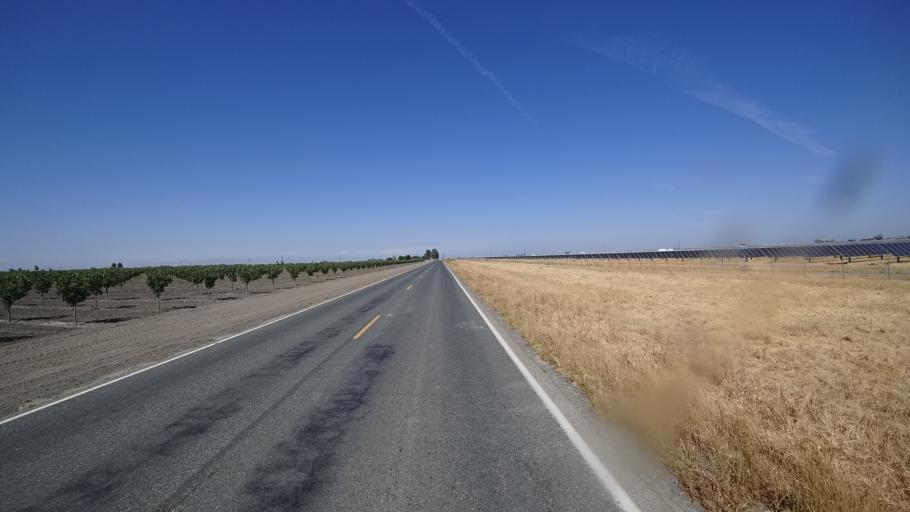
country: US
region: California
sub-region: Kings County
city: Stratford
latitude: 36.2115
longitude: -119.7937
